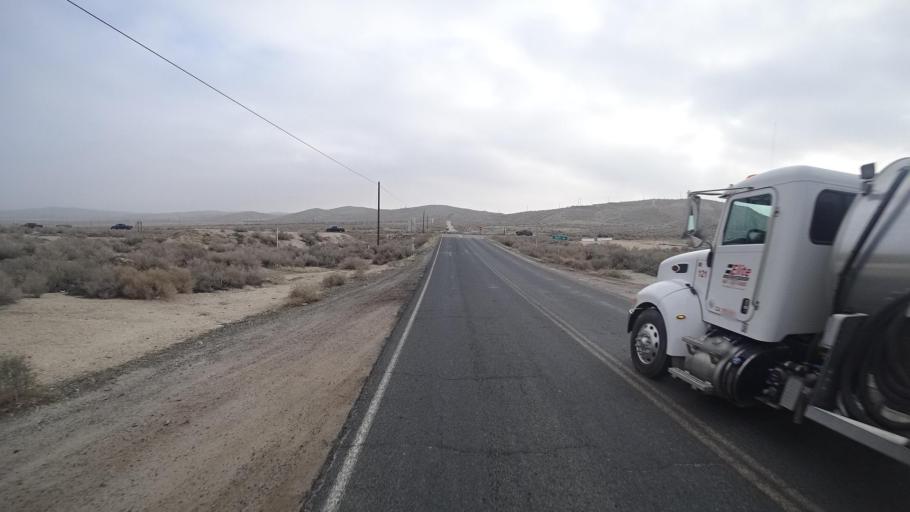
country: US
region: California
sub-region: Kern County
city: Ford City
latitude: 35.1874
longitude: -119.4458
